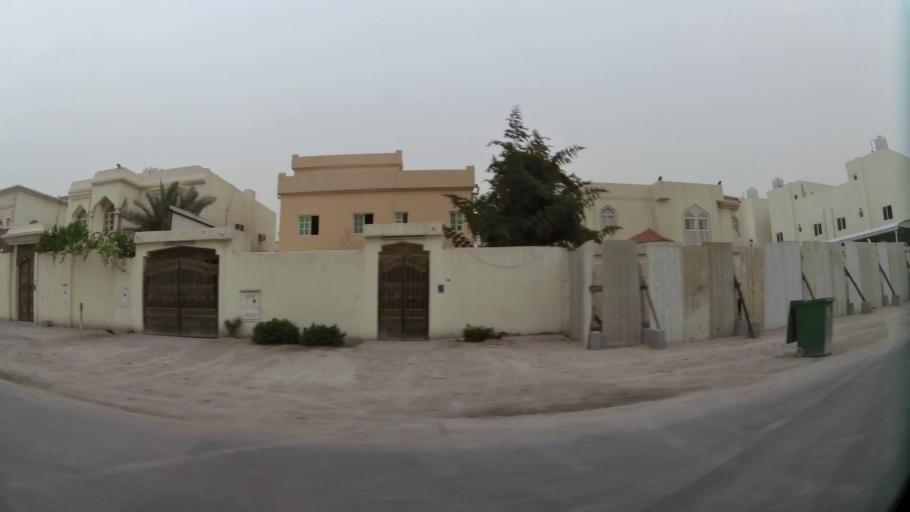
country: QA
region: Baladiyat ad Dawhah
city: Doha
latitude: 25.2363
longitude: 51.4889
